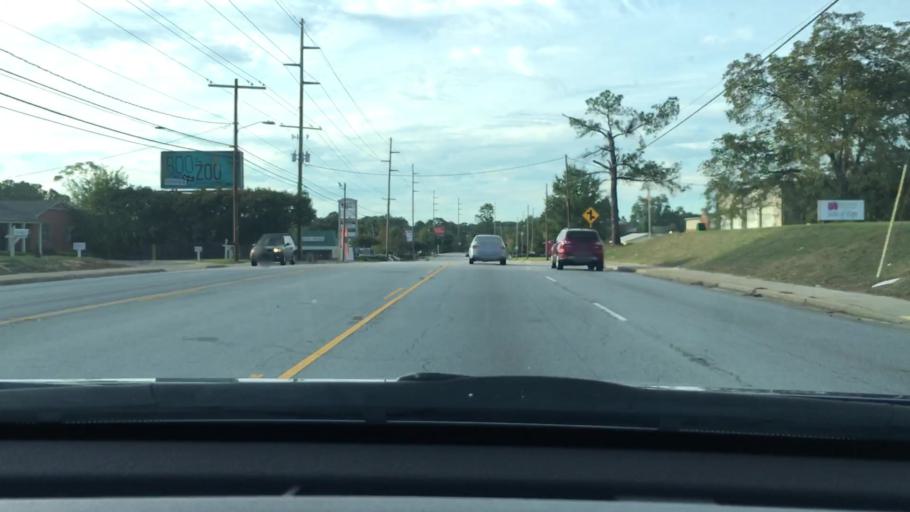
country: US
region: South Carolina
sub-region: Lexington County
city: Saint Andrews
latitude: 34.0516
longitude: -81.1072
